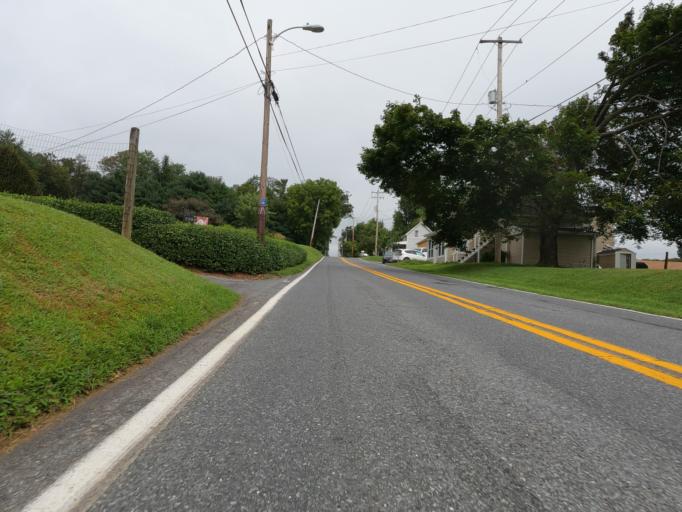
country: US
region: Maryland
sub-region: Carroll County
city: Mount Airy
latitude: 39.3112
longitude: -77.1097
